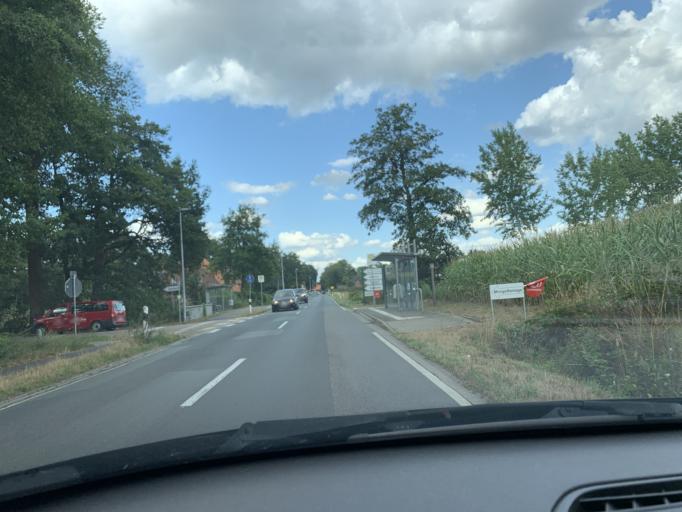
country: DE
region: Lower Saxony
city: Bad Zwischenahn
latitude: 53.1869
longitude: 8.0361
